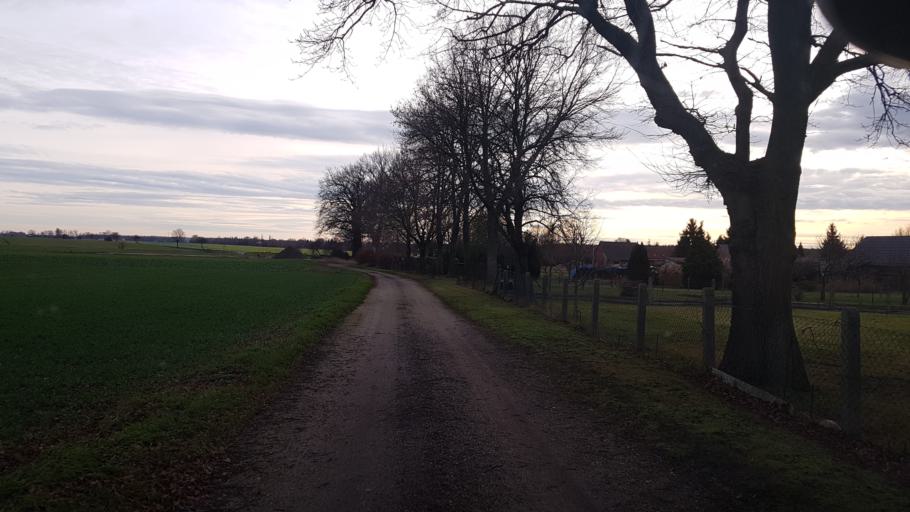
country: DE
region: Brandenburg
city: Doberlug-Kirchhain
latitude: 51.6719
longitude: 13.5129
